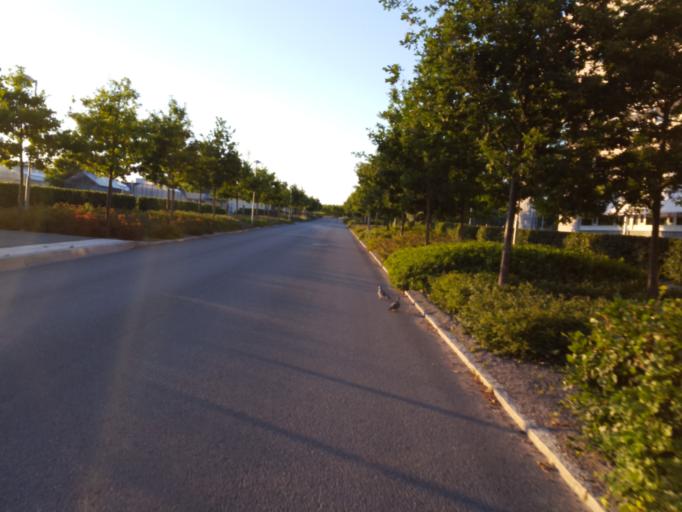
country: SE
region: Uppsala
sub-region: Uppsala Kommun
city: Saevja
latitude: 59.8159
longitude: 17.6592
